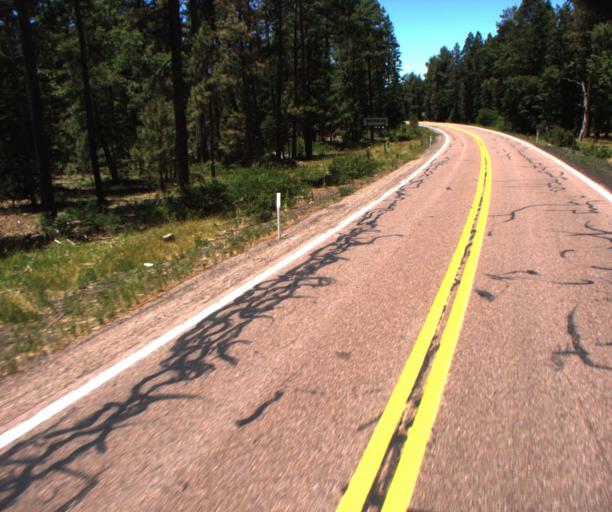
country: US
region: Arizona
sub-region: Gila County
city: Pine
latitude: 34.4566
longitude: -111.4037
